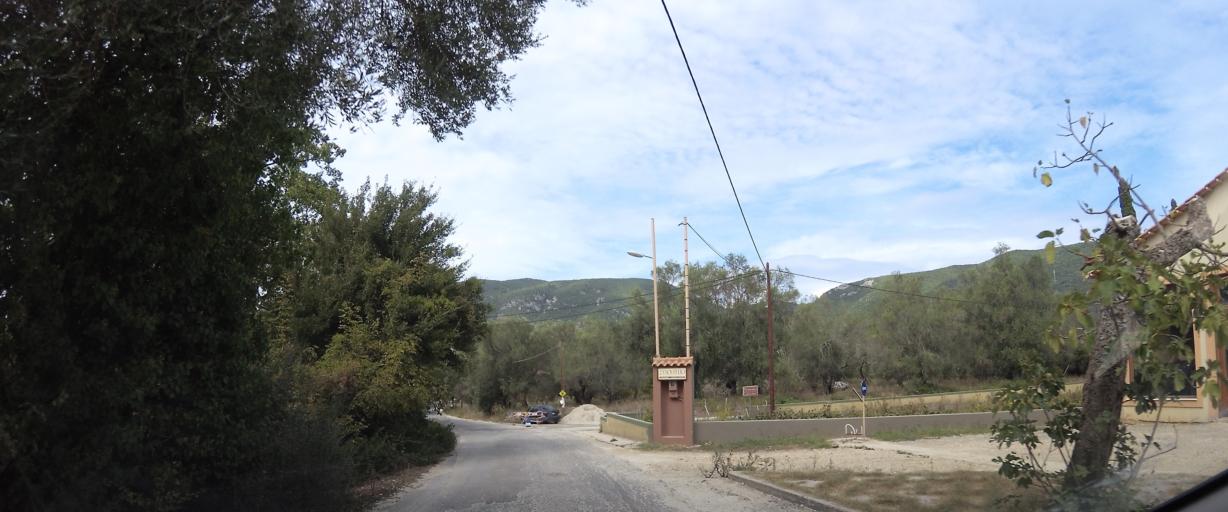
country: GR
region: Ionian Islands
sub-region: Nomos Kerkyras
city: Kontokali
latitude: 39.6972
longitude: 19.8047
